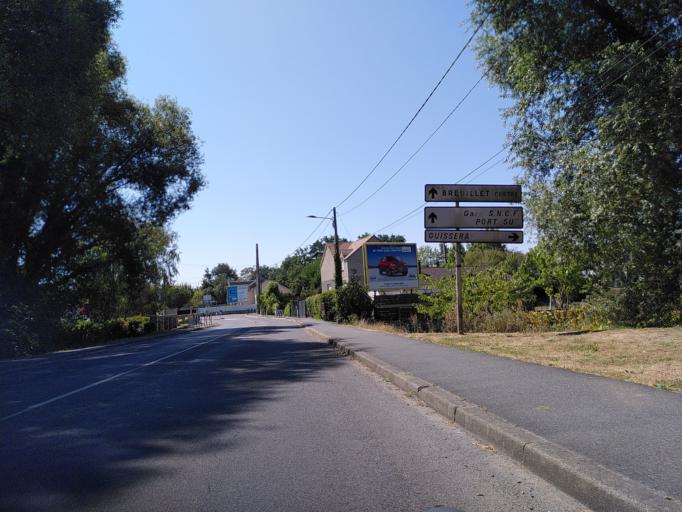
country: FR
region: Ile-de-France
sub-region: Departement de l'Essonne
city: Bruyeres-le-Chatel
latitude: 48.5796
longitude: 2.1937
